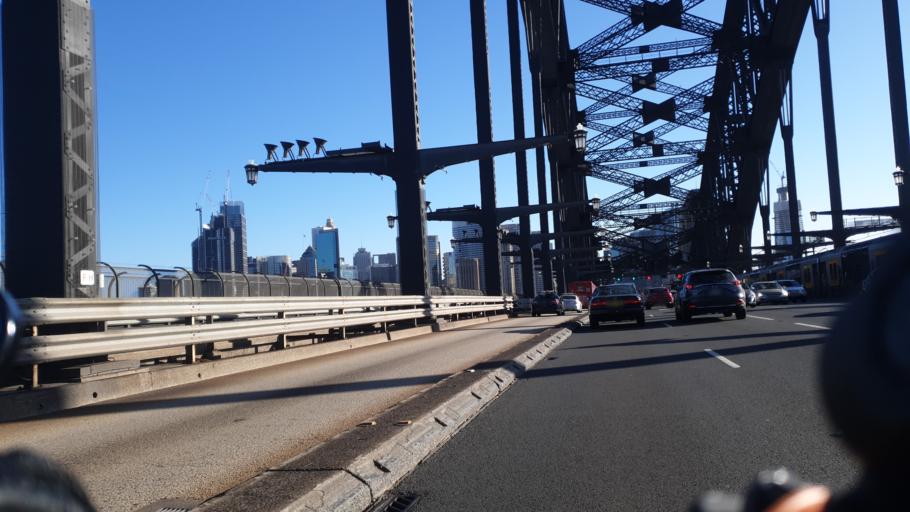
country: AU
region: New South Wales
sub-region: North Sydney
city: Kirribilli
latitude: -33.8526
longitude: 151.2109
